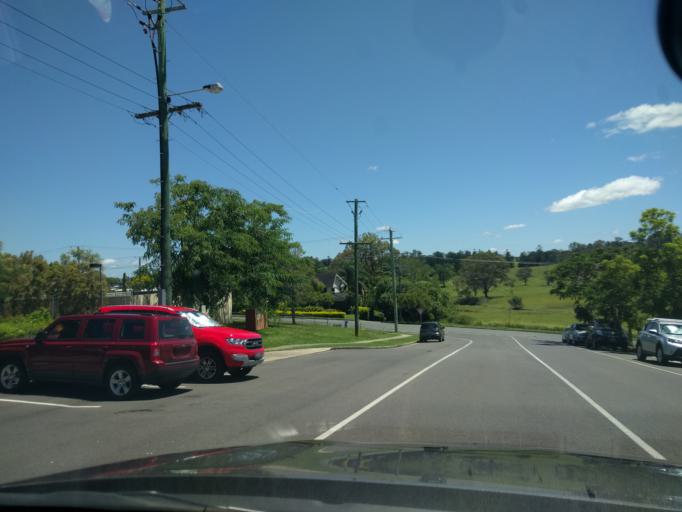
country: AU
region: Queensland
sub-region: Logan
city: Cedar Vale
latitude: -27.9846
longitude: 153.0031
